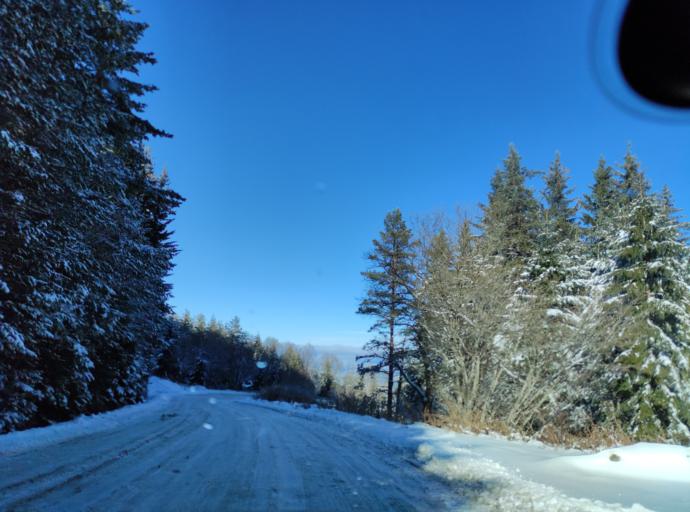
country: BG
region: Sofia-Capital
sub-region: Stolichna Obshtina
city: Sofia
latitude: 42.5915
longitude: 23.2967
